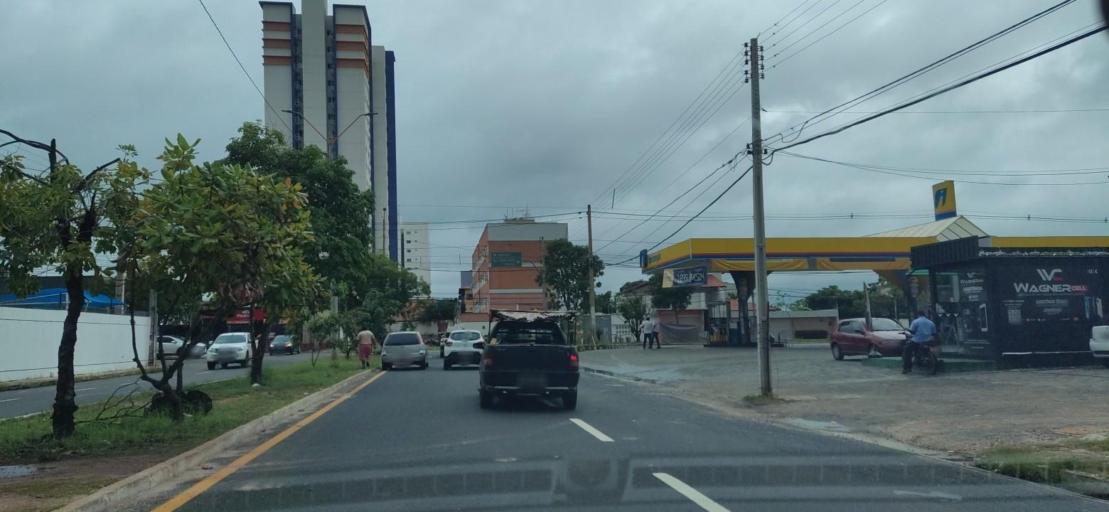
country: BR
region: Piaui
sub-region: Teresina
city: Teresina
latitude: -5.0704
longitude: -42.7501
